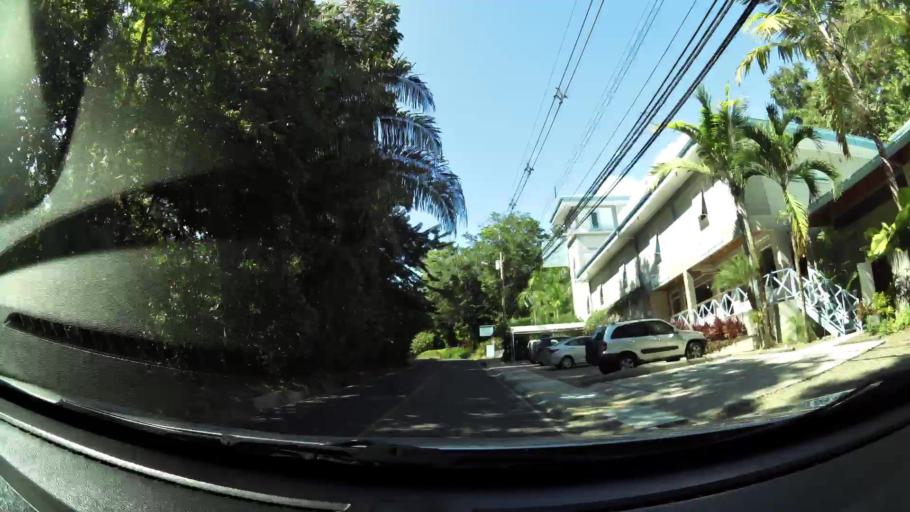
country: CR
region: Puntarenas
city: Quepos
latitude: 9.4194
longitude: -84.1583
